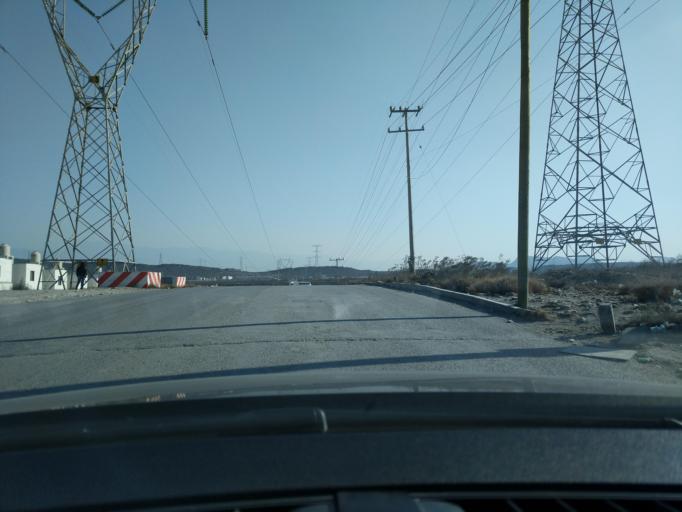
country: MX
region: Coahuila
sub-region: Ramos Arizpe
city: Ramos Arizpe
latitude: 25.5408
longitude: -100.9780
